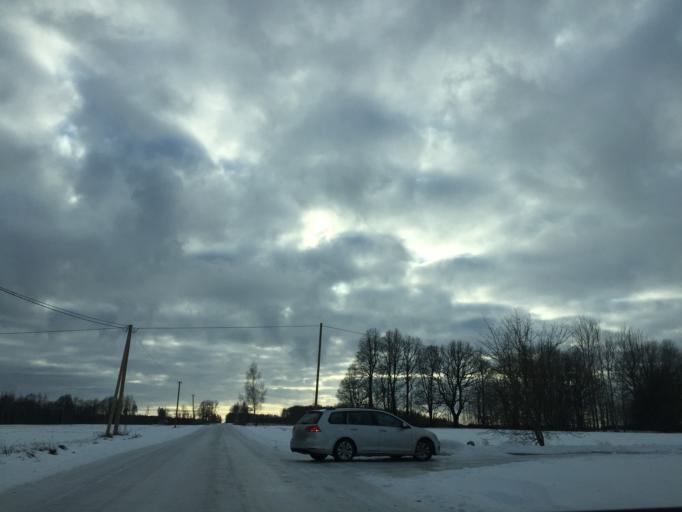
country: LV
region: Lielvarde
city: Lielvarde
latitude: 56.5598
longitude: 24.7355
